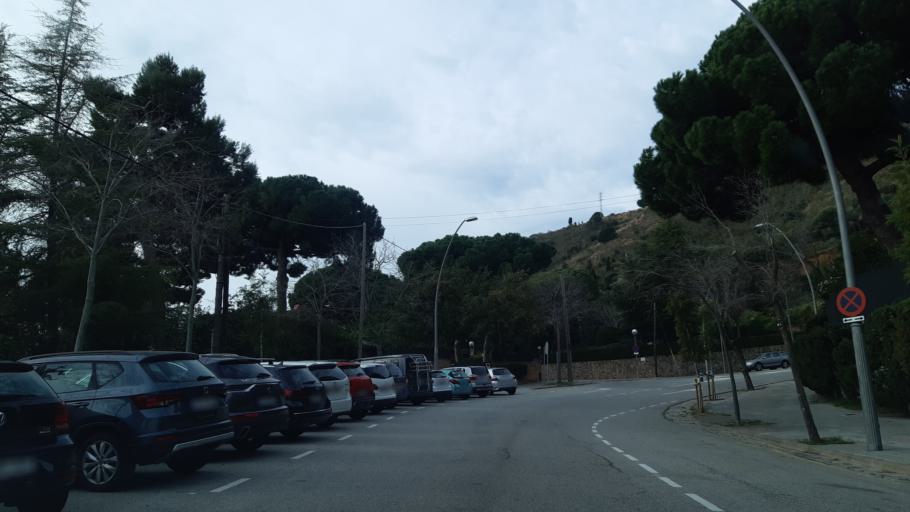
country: ES
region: Catalonia
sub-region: Provincia de Barcelona
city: Esplugues de Llobregat
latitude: 41.3918
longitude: 2.1046
